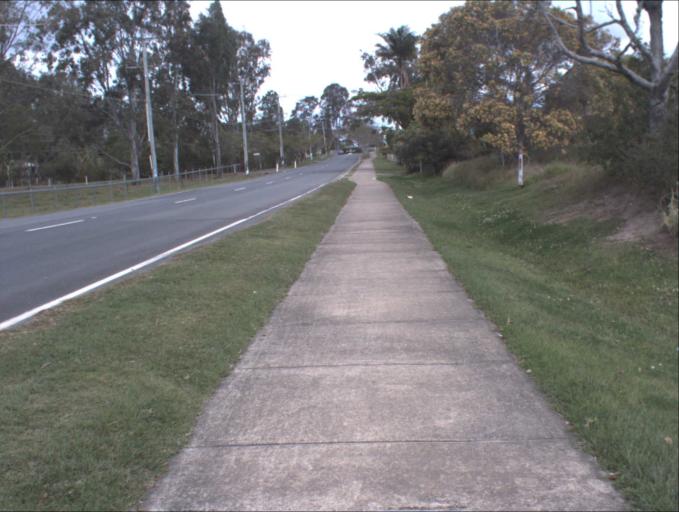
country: AU
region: Queensland
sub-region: Logan
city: Waterford West
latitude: -27.6977
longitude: 153.1352
